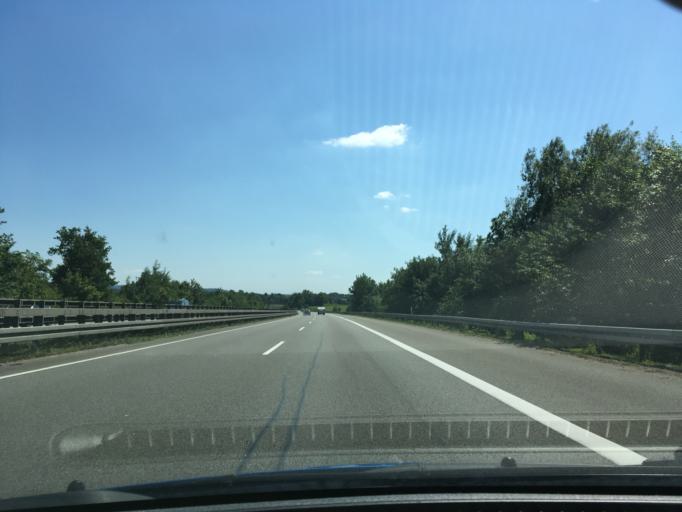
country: DE
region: Lower Saxony
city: Bissendorf
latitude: 52.2162
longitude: 8.2439
